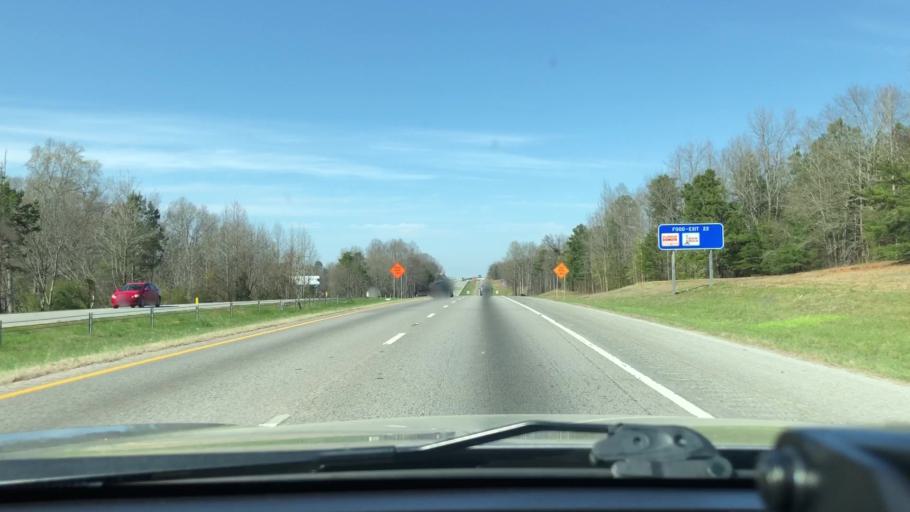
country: US
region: South Carolina
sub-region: Spartanburg County
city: Roebuck
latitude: 34.9030
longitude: -81.9913
